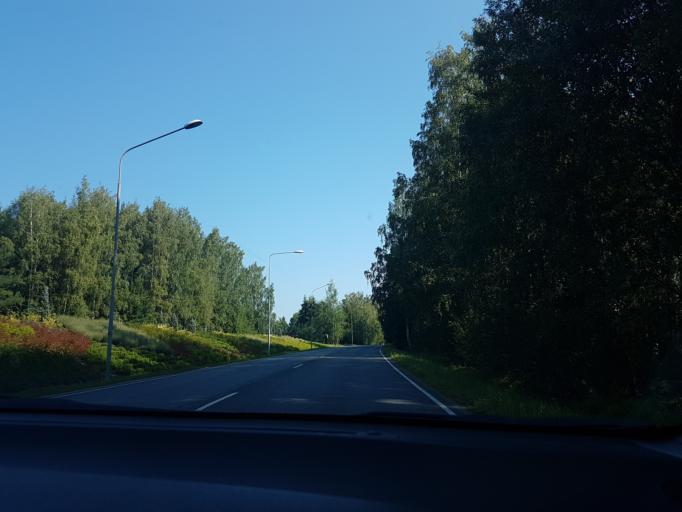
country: FI
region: Uusimaa
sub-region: Helsinki
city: Kerava
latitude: 60.3873
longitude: 25.0987
